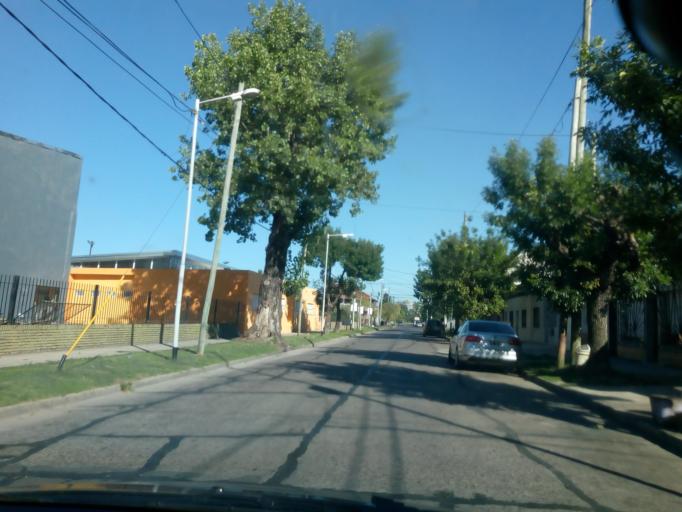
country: AR
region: Buenos Aires
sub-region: Partido de Avellaneda
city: Avellaneda
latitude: -34.6795
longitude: -58.3587
